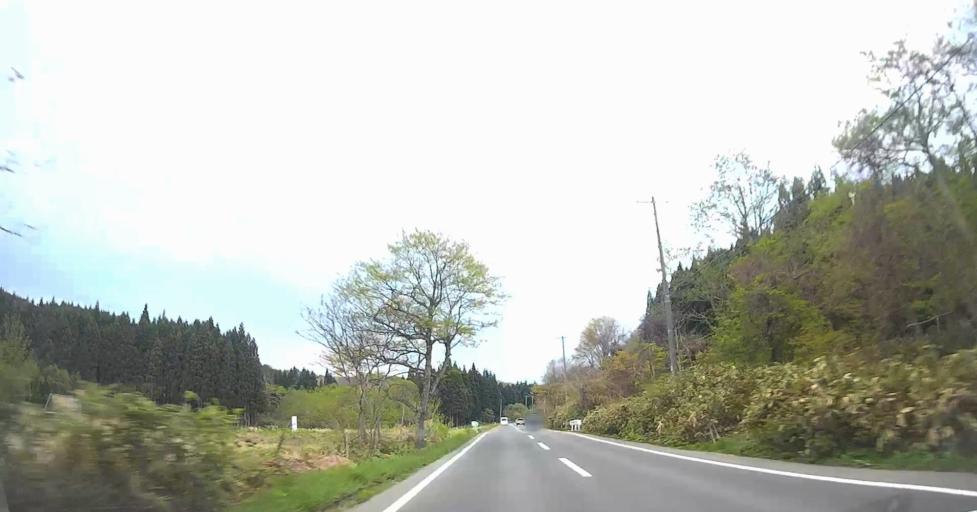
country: JP
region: Aomori
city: Goshogawara
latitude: 41.1226
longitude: 140.5217
